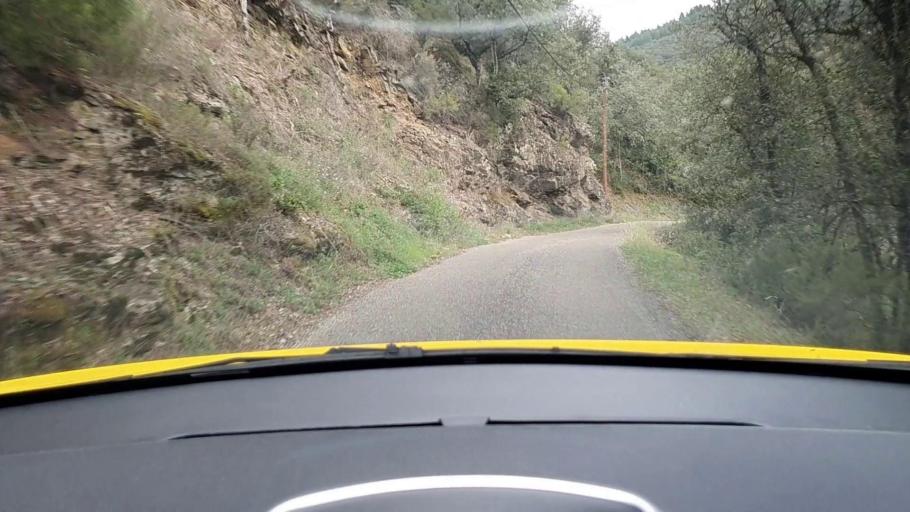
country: FR
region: Languedoc-Roussillon
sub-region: Departement du Gard
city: Sumene
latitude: 44.0137
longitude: 3.6607
